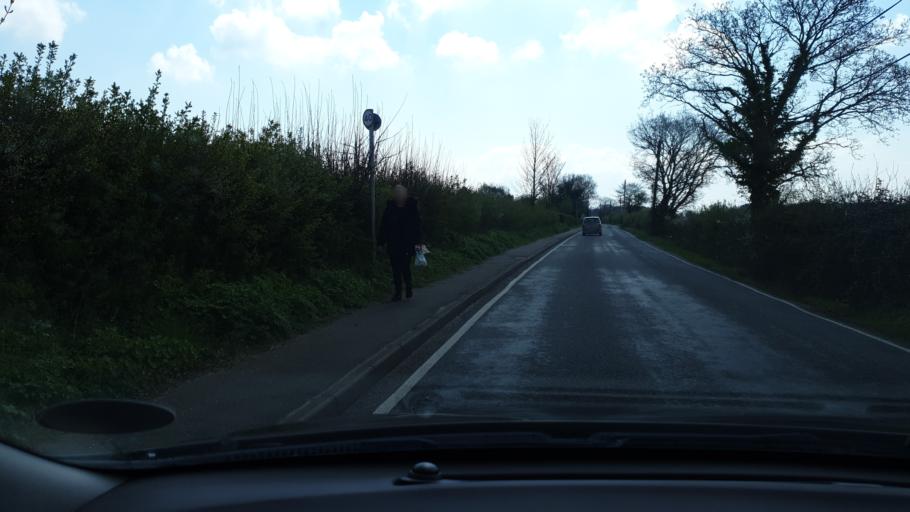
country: GB
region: England
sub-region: Essex
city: Great Bentley
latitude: 51.8455
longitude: 1.0682
